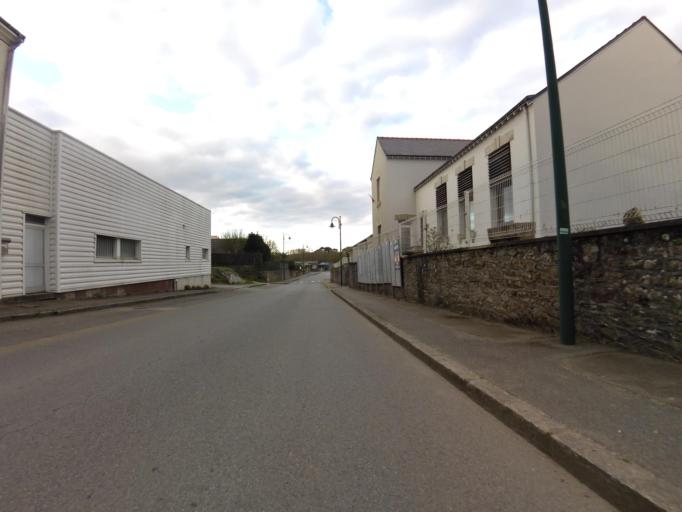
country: FR
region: Brittany
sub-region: Departement du Morbihan
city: Plougoumelen
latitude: 47.6536
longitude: -2.9169
